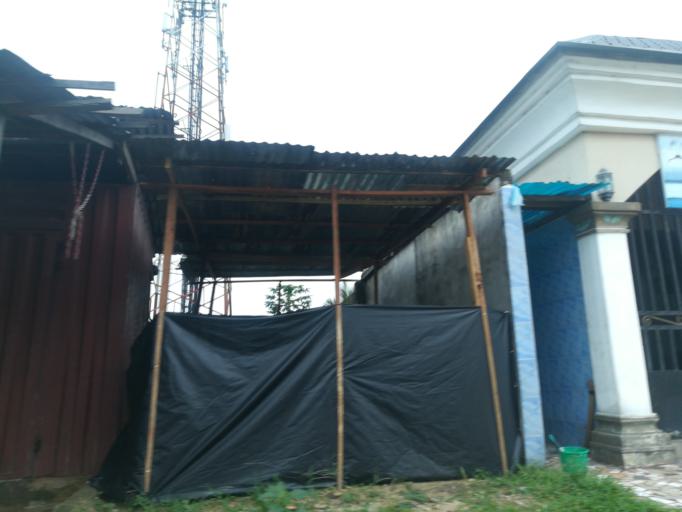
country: NG
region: Rivers
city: Port Harcourt
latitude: 4.8488
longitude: 6.9775
